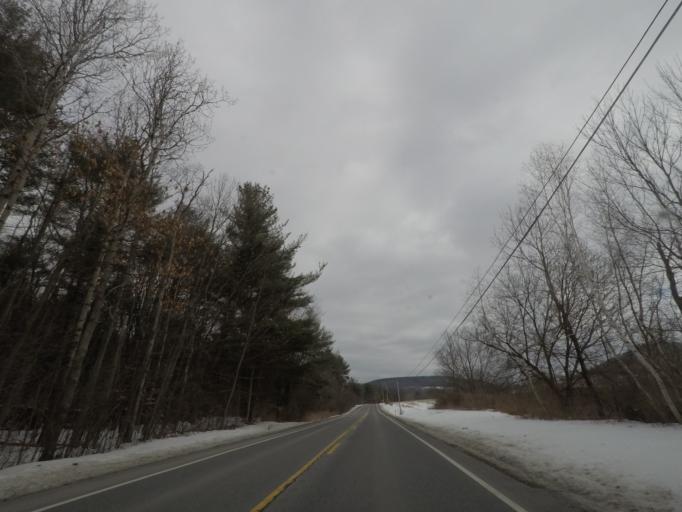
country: US
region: New York
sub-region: Washington County
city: Greenwich
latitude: 43.0666
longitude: -73.4686
